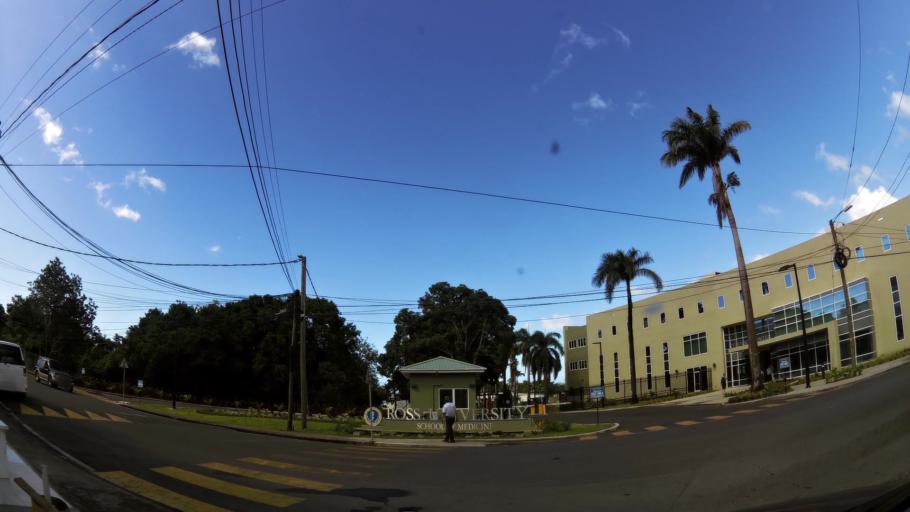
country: DM
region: Saint John
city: Portsmouth
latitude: 15.5560
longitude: -61.4585
